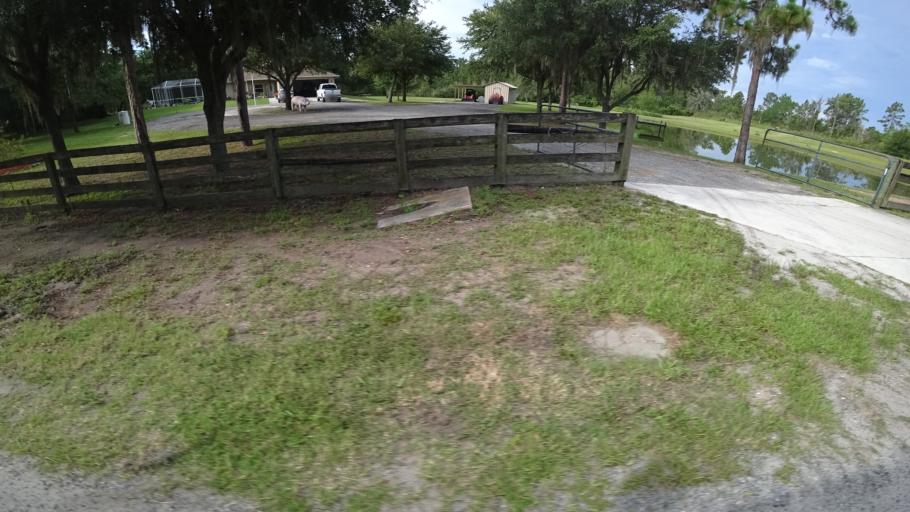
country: US
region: Florida
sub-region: Sarasota County
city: Fruitville
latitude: 27.4088
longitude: -82.2807
